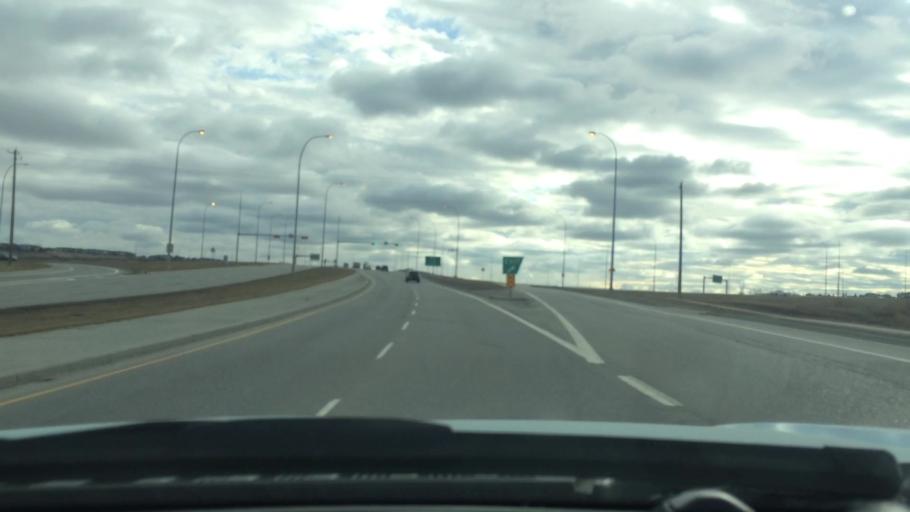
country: CA
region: Alberta
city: Calgary
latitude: 51.1582
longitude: -114.1208
